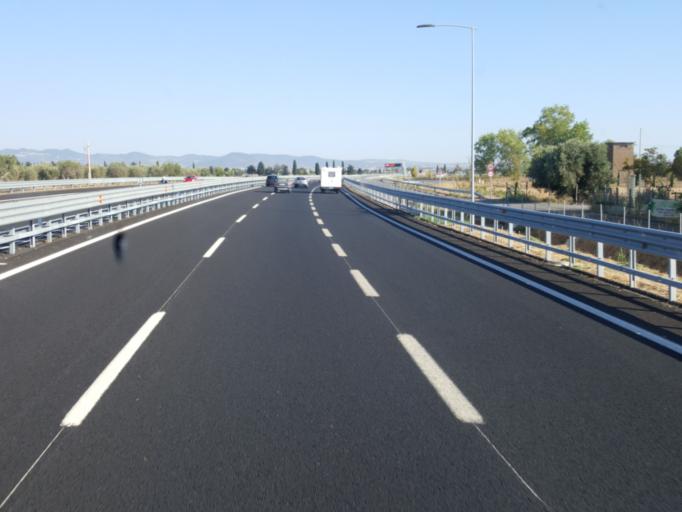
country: IT
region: Latium
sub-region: Provincia di Viterbo
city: Tarquinia
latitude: 42.2335
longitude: 11.7640
